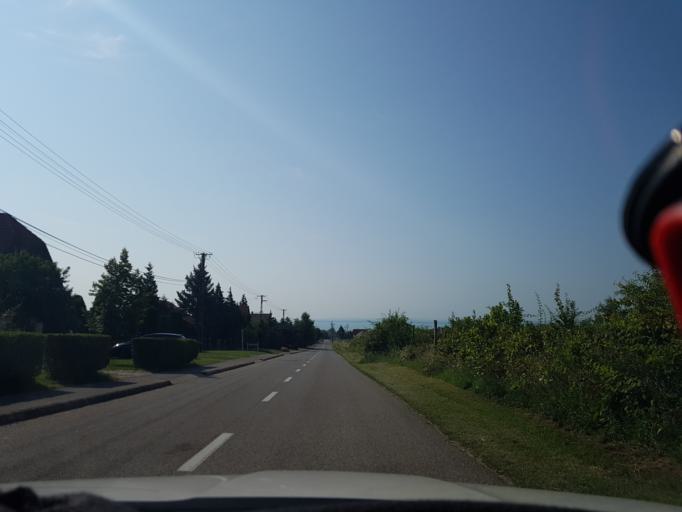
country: HU
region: Veszprem
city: Csopak
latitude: 46.9932
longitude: 17.9671
